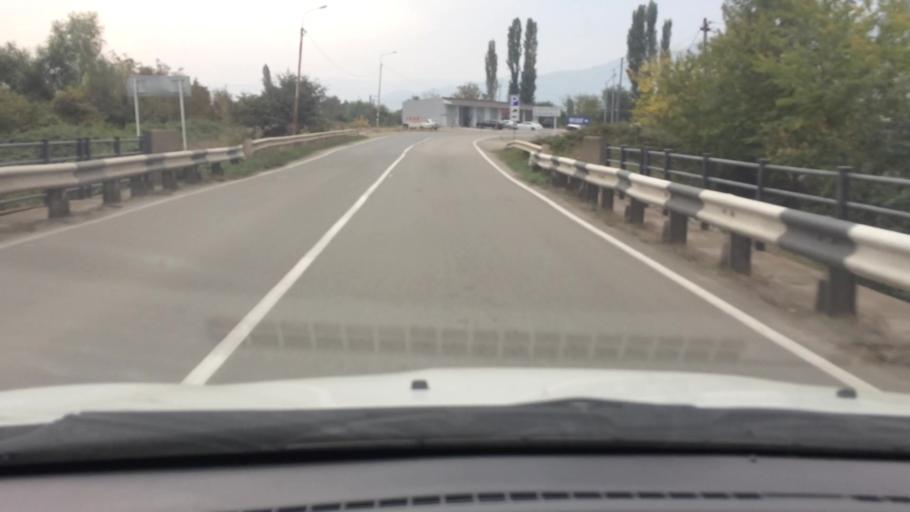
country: AM
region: Tavush
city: Bagratashen
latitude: 41.2552
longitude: 44.7990
